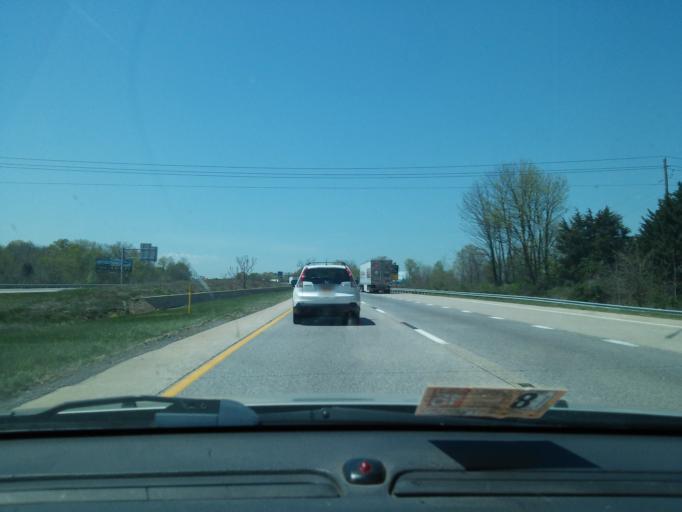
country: US
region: Pennsylvania
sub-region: Dauphin County
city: Skyline View
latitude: 40.3781
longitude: -76.6684
